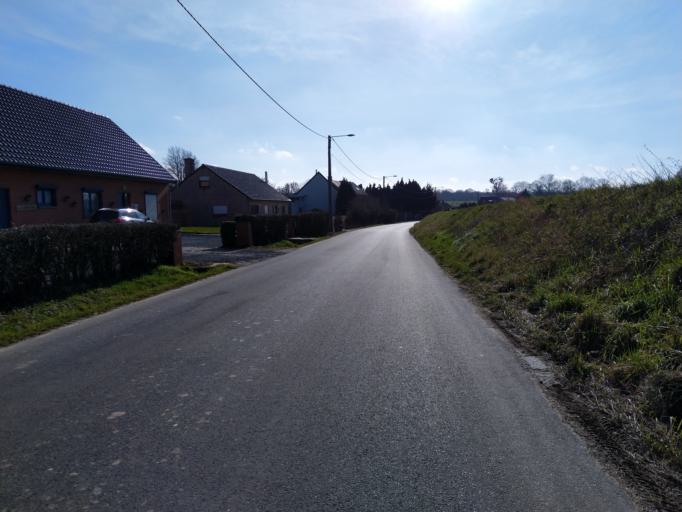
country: FR
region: Nord-Pas-de-Calais
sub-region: Departement du Nord
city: Feignies
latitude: 50.3368
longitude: 3.8986
